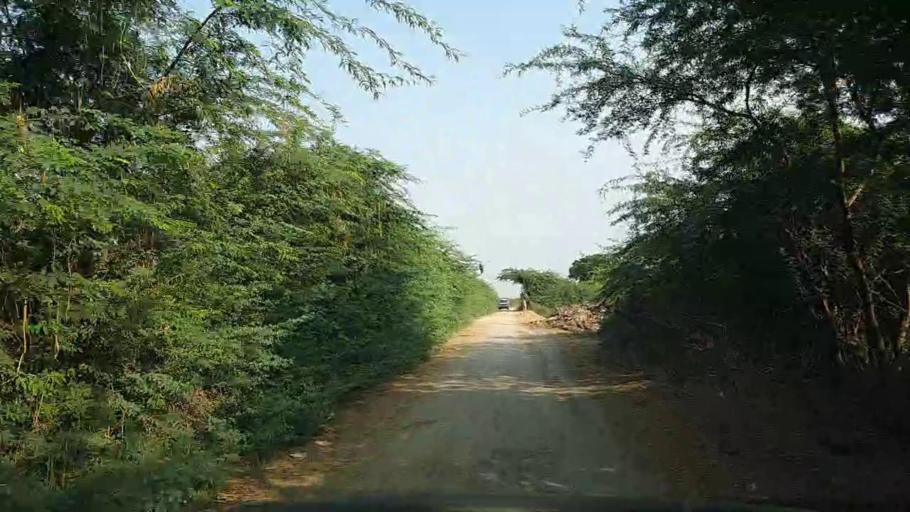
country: PK
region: Sindh
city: Thatta
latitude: 24.6460
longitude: 67.9360
